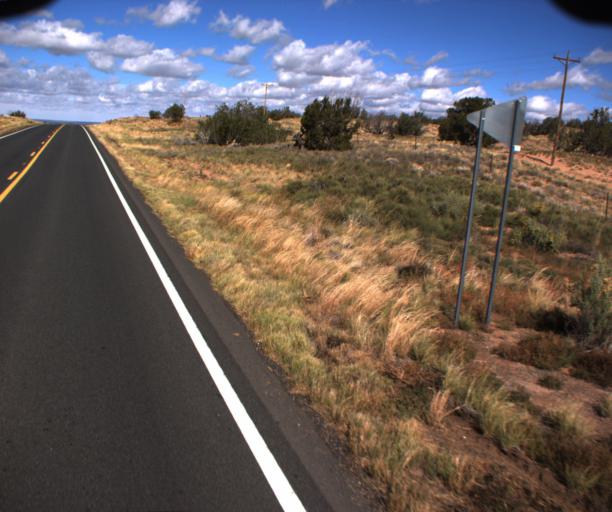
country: US
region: Arizona
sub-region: Apache County
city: Houck
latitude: 35.0763
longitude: -109.2965
